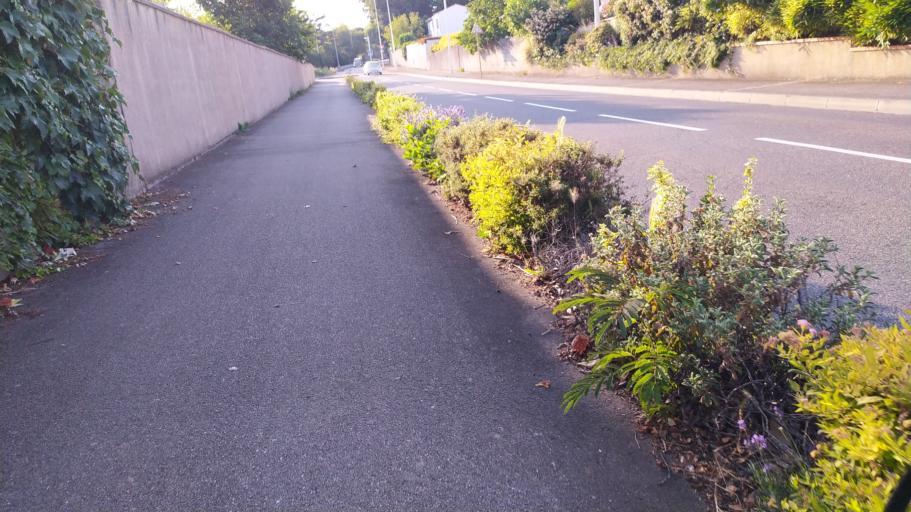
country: FR
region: Midi-Pyrenees
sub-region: Departement de la Haute-Garonne
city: Tournefeuille
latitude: 43.5845
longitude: 1.3265
